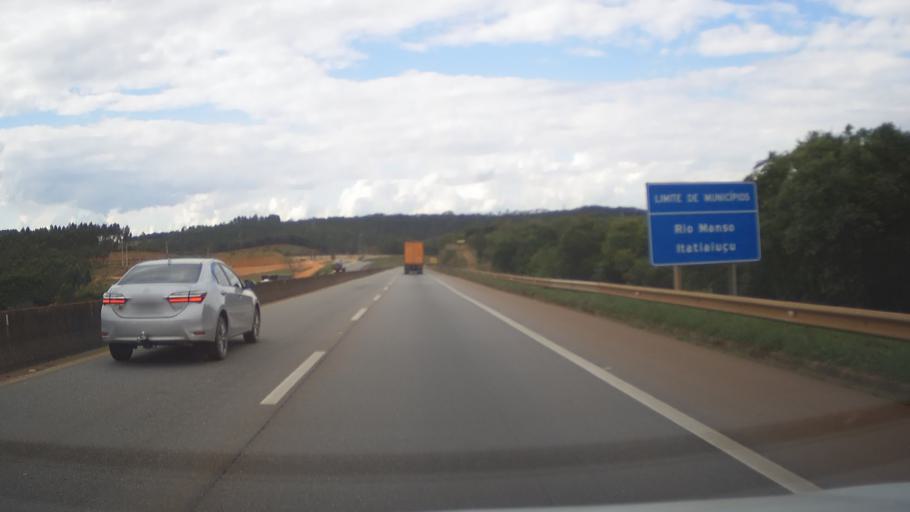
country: BR
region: Minas Gerais
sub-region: Itauna
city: Itauna
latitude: -20.2903
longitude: -44.4361
